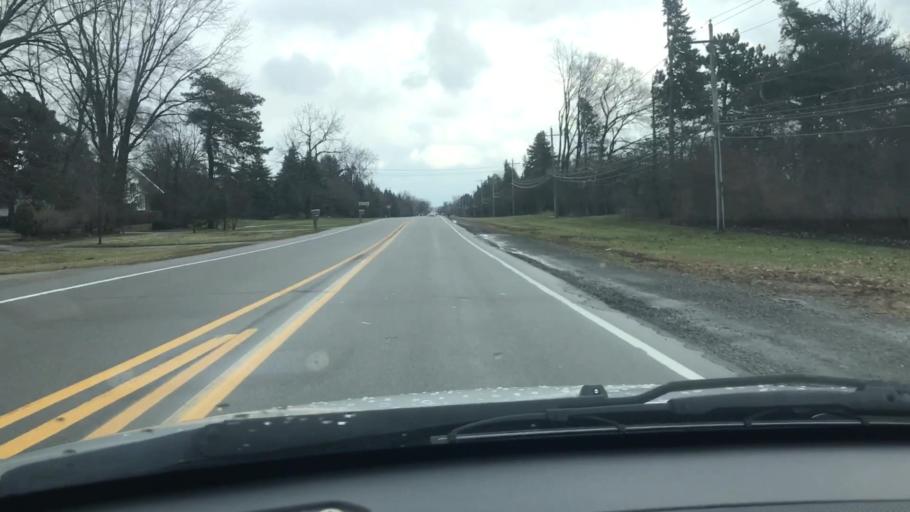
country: US
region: Michigan
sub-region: Oakland County
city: Birmingham
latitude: 42.5763
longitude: -83.1859
